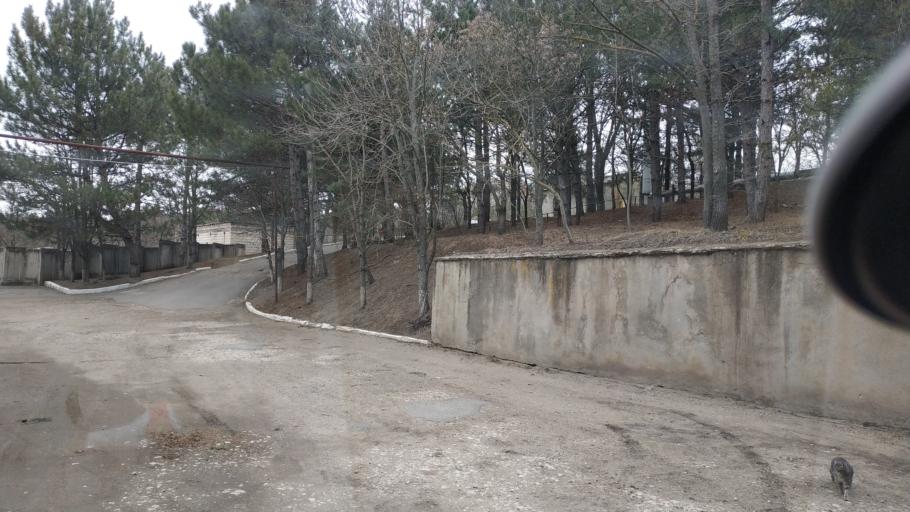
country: MD
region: Telenesti
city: Cocieri
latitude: 47.3323
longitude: 29.0839
